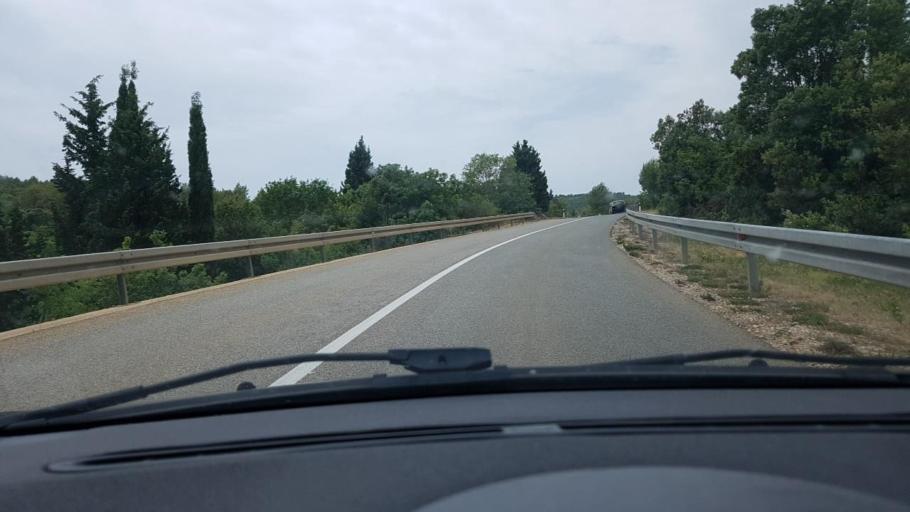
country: HR
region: Dubrovacko-Neretvanska
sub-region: Grad Korcula
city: Zrnovo
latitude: 42.9372
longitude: 17.0872
